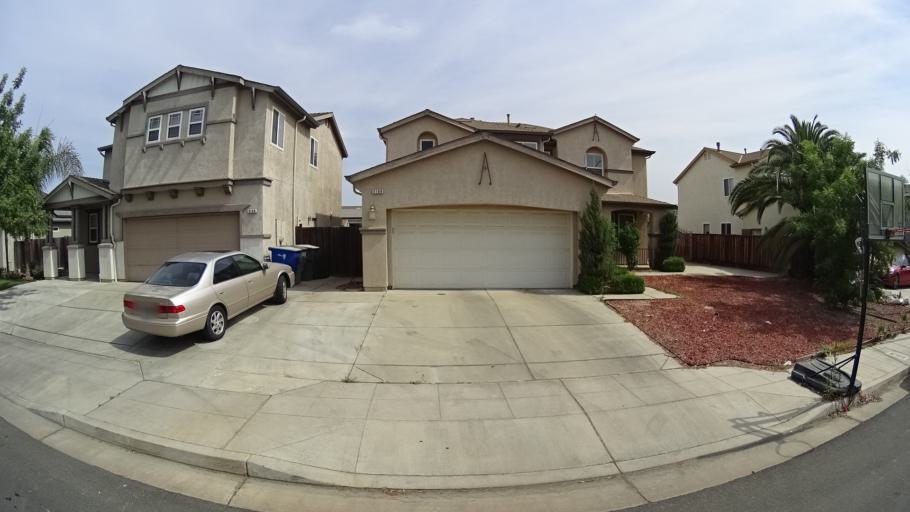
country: US
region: California
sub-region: Fresno County
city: West Park
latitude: 36.7626
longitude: -119.8836
